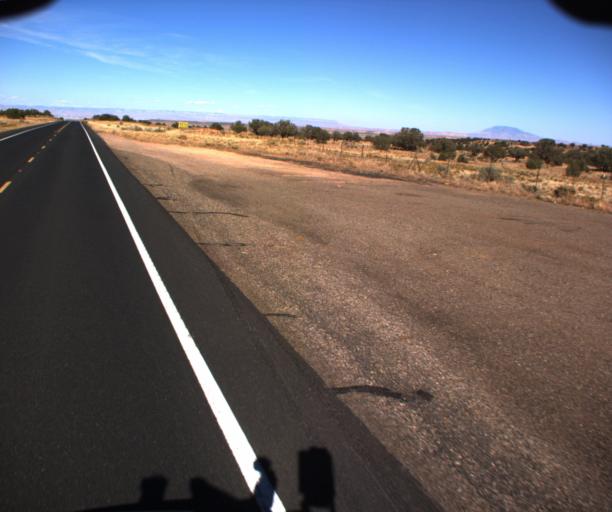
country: US
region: Arizona
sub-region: Coconino County
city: LeChee
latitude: 36.7056
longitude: -111.5972
